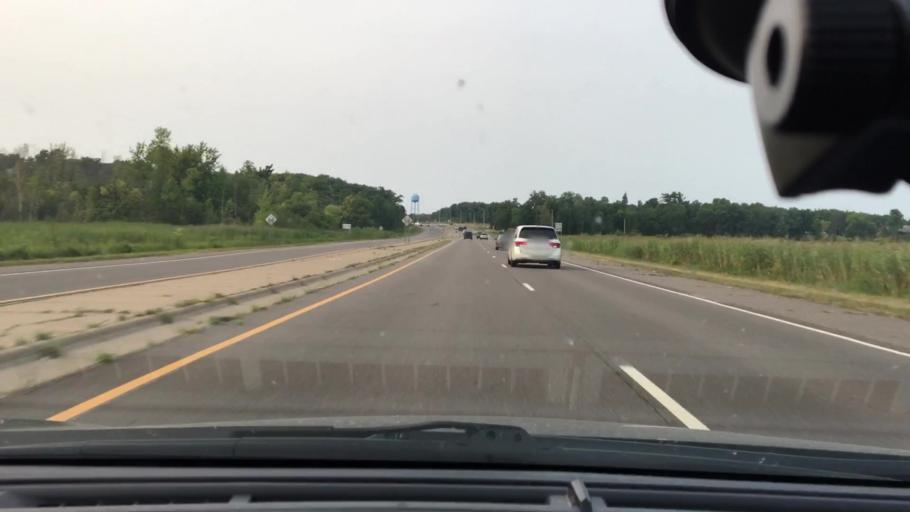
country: US
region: Minnesota
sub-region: Mille Lacs County
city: Vineland
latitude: 46.1721
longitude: -93.7581
